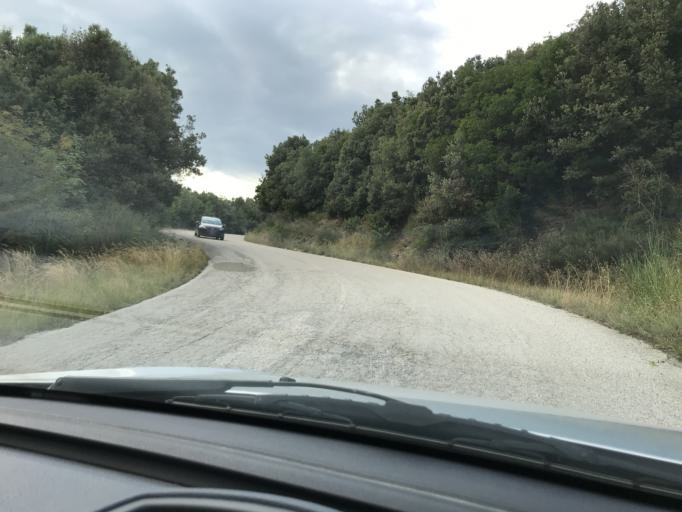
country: IT
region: Umbria
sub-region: Provincia di Terni
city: Montecchio
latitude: 42.6868
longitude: 12.2978
